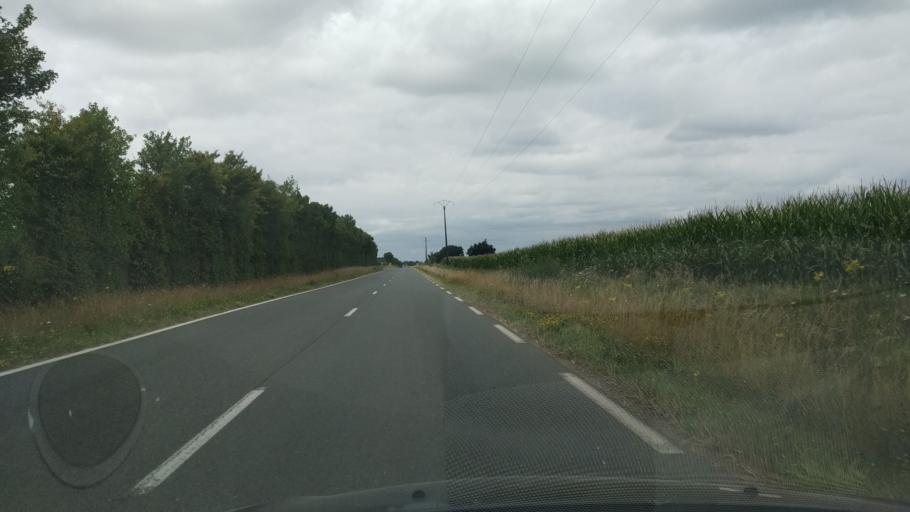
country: FR
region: Poitou-Charentes
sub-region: Departement de la Vienne
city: La Villedieu-du-Clain
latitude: 46.4150
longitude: 0.3861
